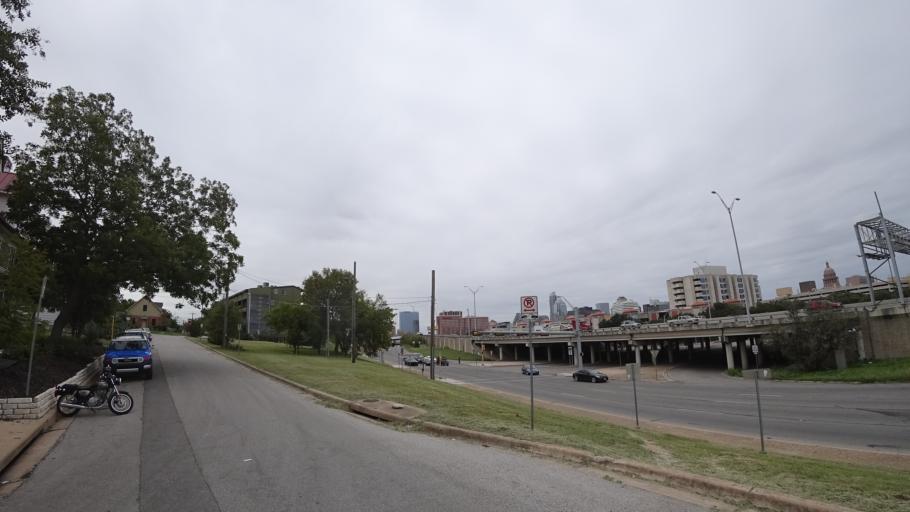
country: US
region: Texas
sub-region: Travis County
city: Austin
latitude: 30.2751
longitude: -97.7306
